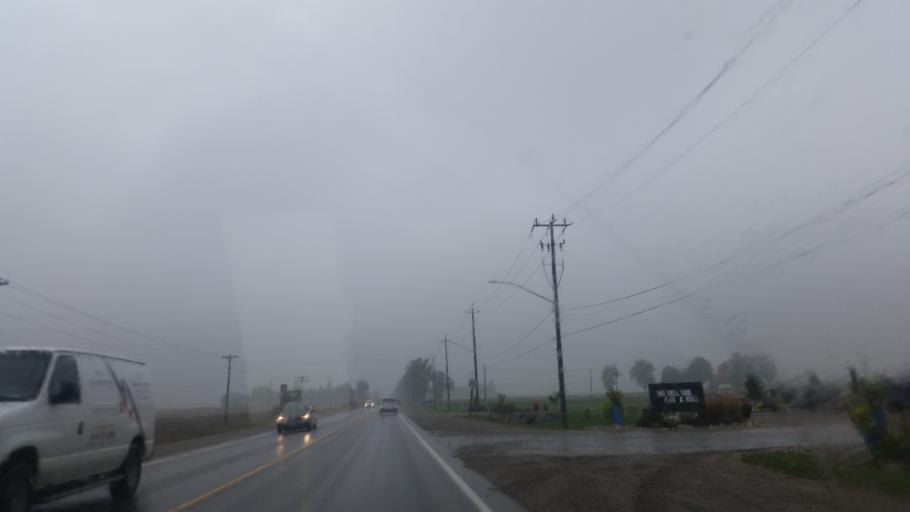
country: CA
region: Ontario
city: Stratford
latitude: 43.3421
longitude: -81.0077
